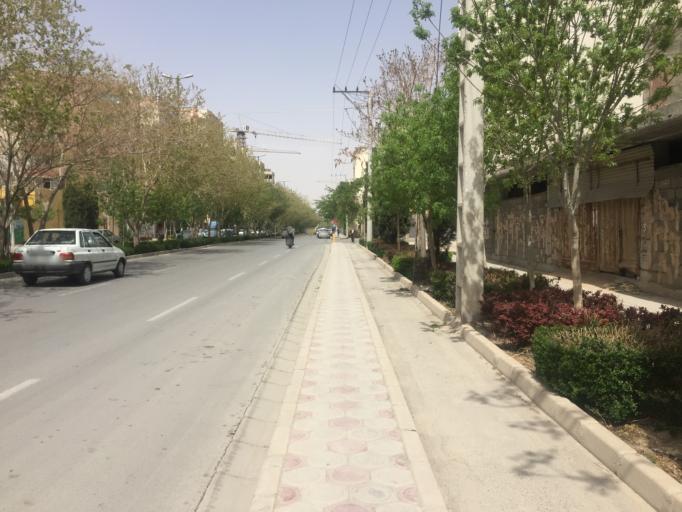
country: IR
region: Isfahan
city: Isfahan
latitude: 32.6986
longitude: 51.6792
